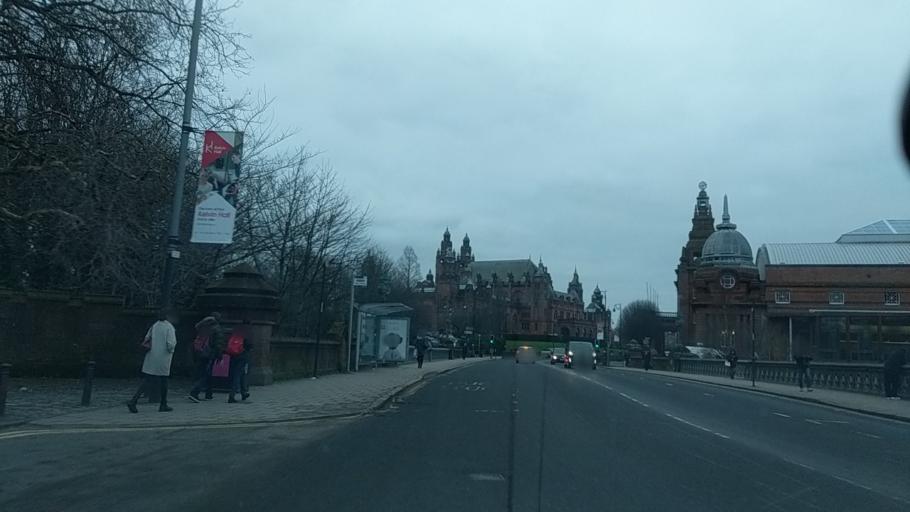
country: GB
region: Scotland
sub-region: Glasgow City
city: Glasgow
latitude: 55.8699
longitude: -4.2950
